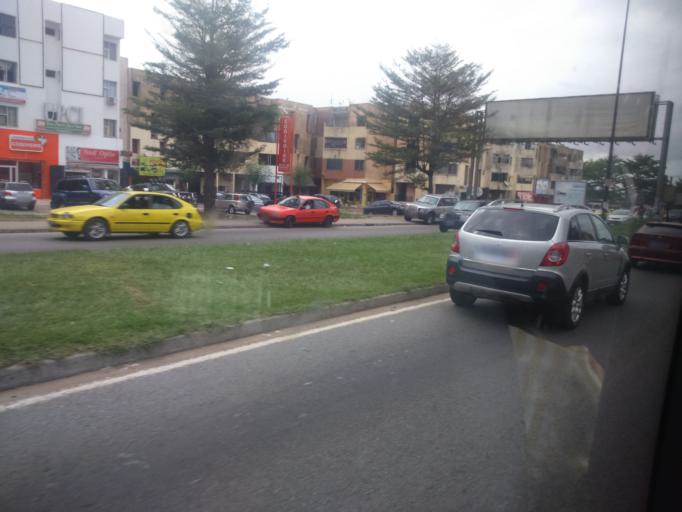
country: CI
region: Lagunes
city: Abobo
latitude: 5.3697
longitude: -3.9983
